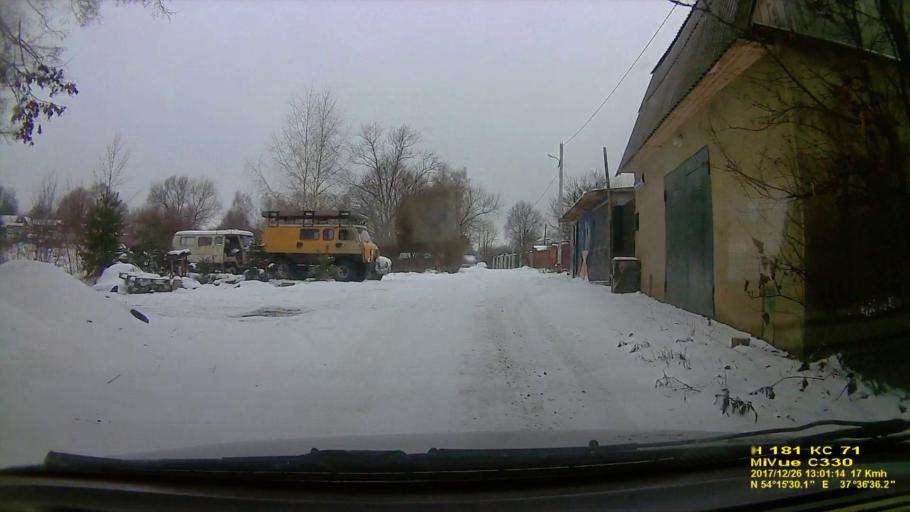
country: RU
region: Tula
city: Gorelki
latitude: 54.2584
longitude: 37.6100
